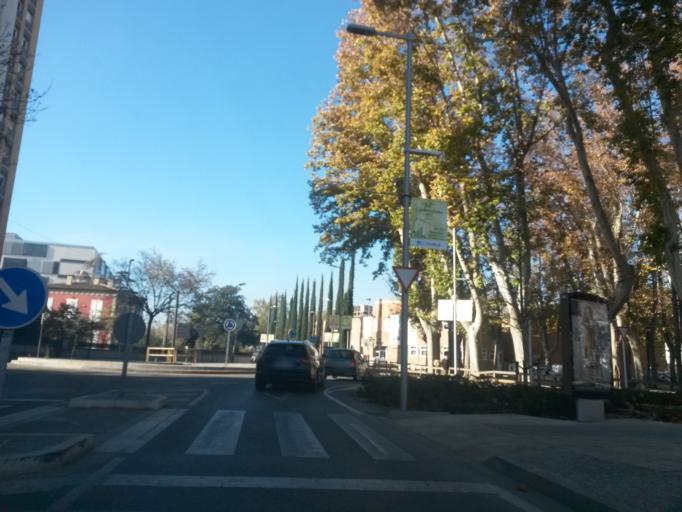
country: ES
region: Catalonia
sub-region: Provincia de Girona
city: Girona
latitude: 41.9845
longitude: 2.8132
